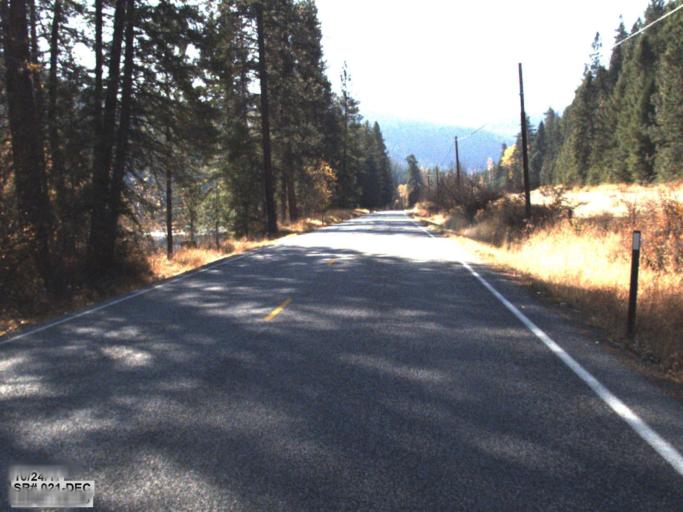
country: CA
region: British Columbia
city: Grand Forks
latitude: 48.9725
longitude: -118.5269
